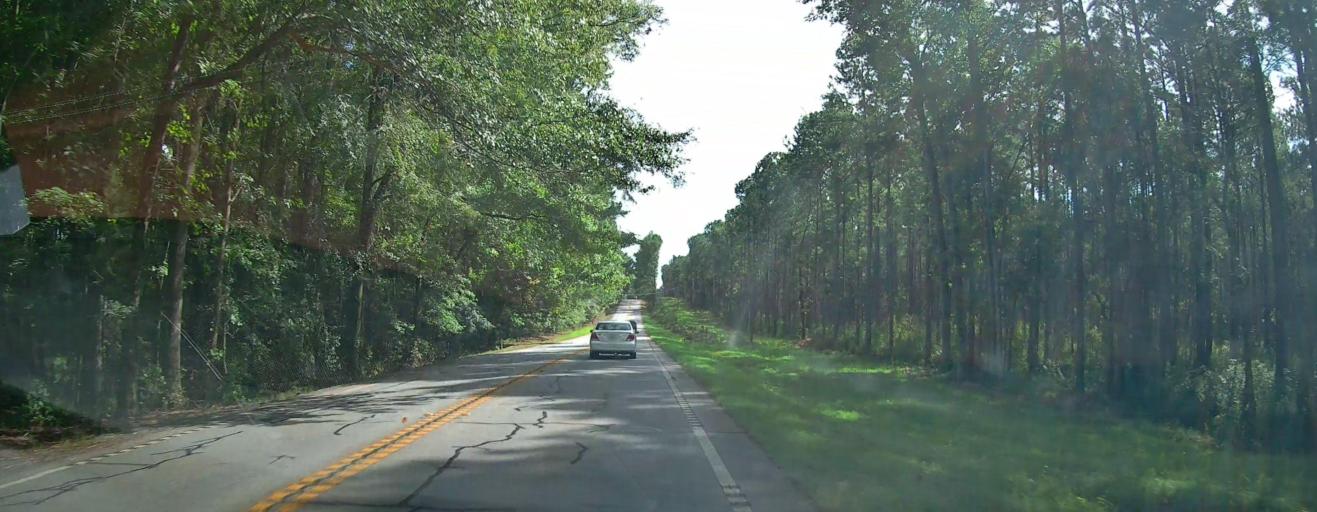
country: US
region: Georgia
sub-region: Harris County
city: Hamilton
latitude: 32.6867
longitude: -84.8571
